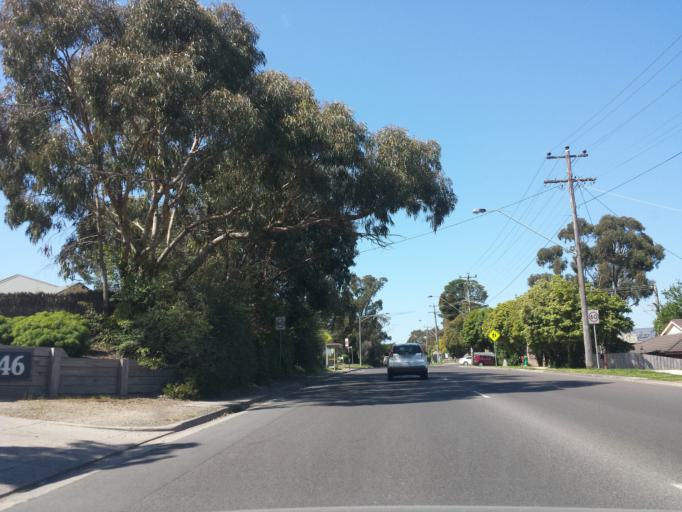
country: AU
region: Victoria
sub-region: Yarra Ranges
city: Mount Evelyn
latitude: -37.7804
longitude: 145.3812
